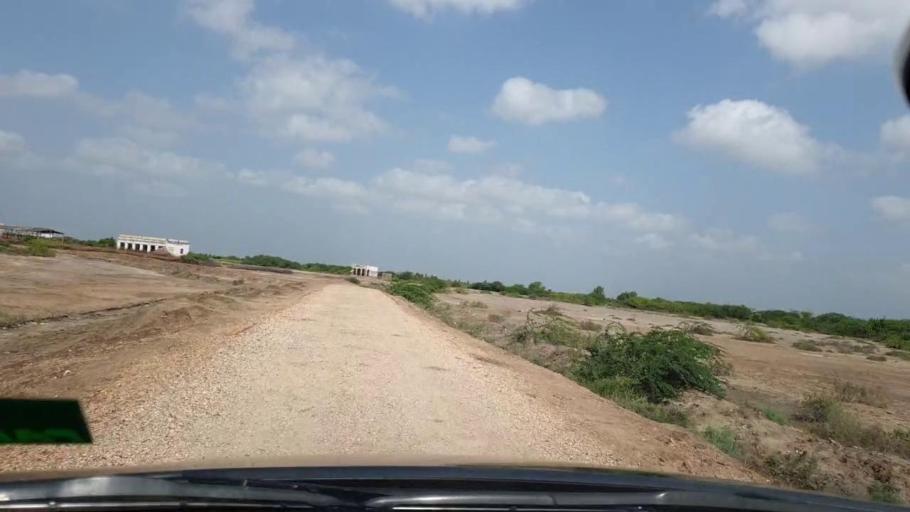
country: PK
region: Sindh
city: Kadhan
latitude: 24.6311
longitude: 69.1445
